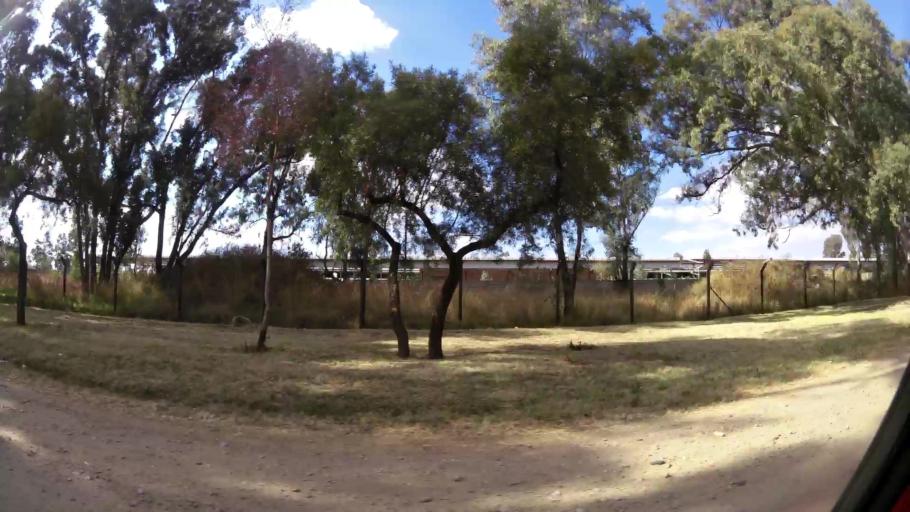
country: ZA
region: Gauteng
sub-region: Ekurhuleni Metropolitan Municipality
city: Tembisa
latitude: -25.9671
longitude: 28.2372
